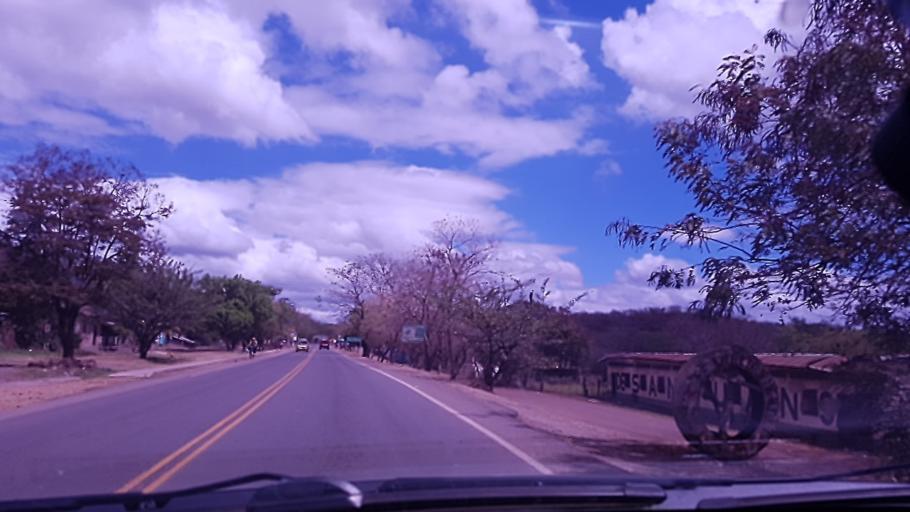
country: NI
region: Esteli
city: Condega
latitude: 13.3694
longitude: -86.3989
